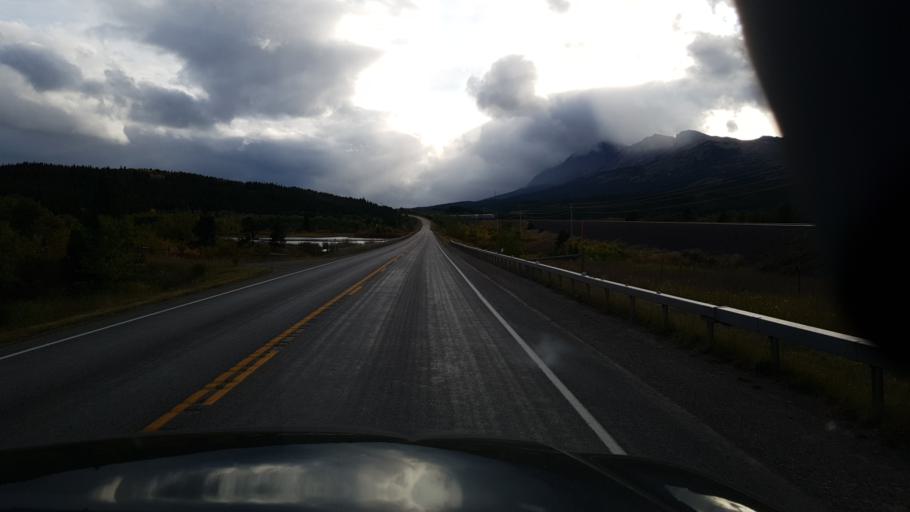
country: US
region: Montana
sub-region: Glacier County
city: South Browning
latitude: 48.3888
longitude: -113.2615
